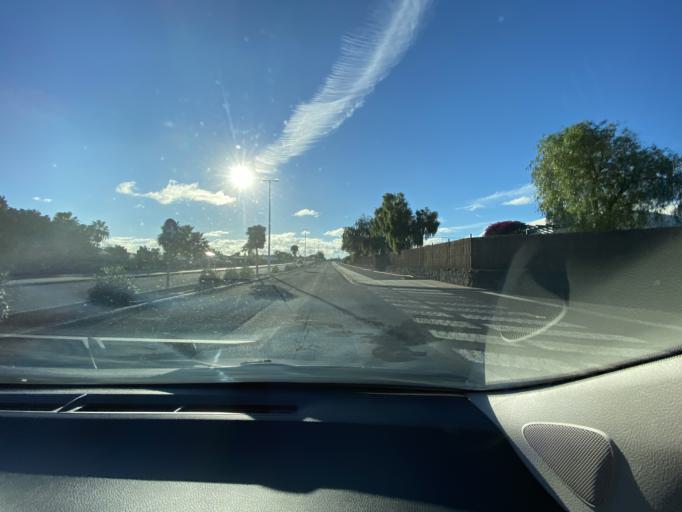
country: ES
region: Canary Islands
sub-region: Provincia de Las Palmas
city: Playa Blanca
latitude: 28.8675
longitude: -13.8350
